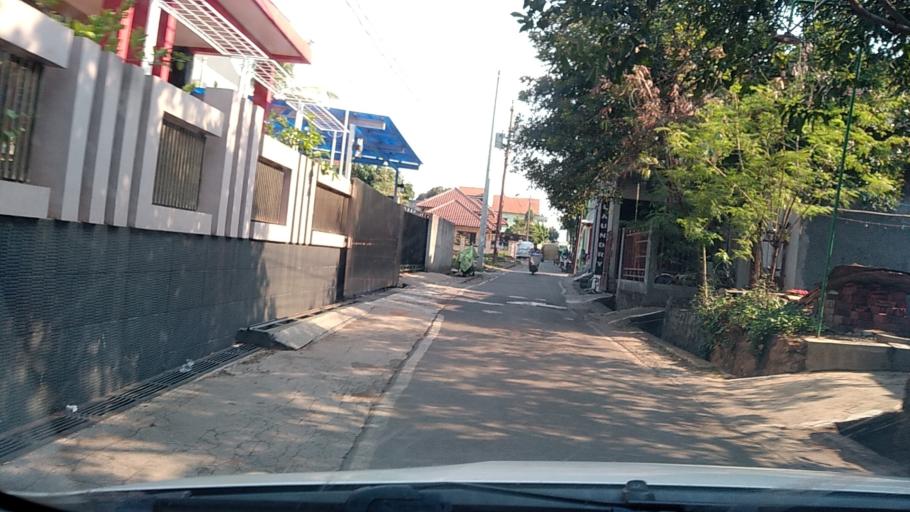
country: ID
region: Central Java
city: Semarang
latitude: -7.0587
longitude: 110.4439
